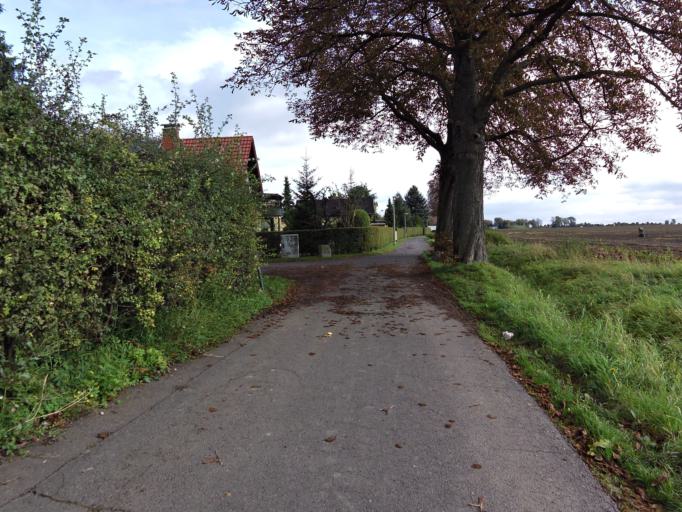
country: DE
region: Saxony
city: Grossposna
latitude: 51.2842
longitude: 12.4355
